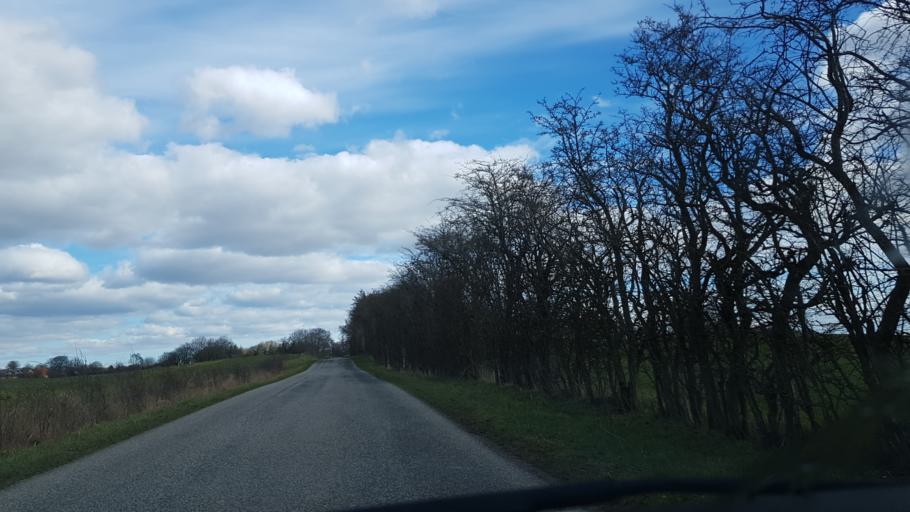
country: DK
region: South Denmark
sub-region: Kolding Kommune
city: Christiansfeld
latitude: 55.3571
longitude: 9.4299
